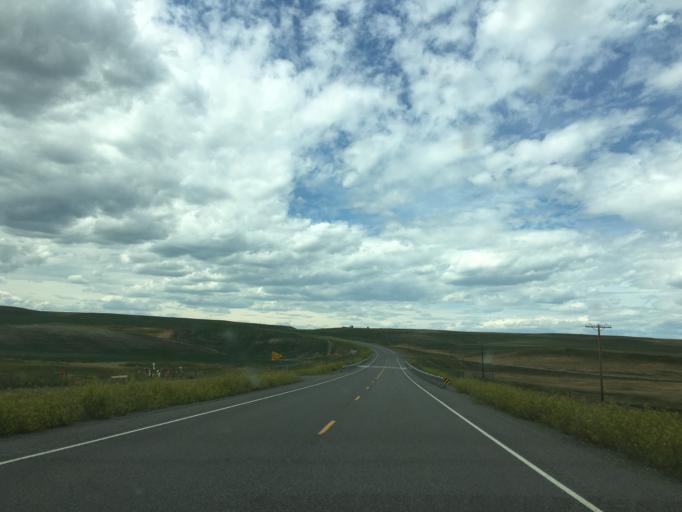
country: US
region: Montana
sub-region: Teton County
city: Choteau
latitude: 48.0849
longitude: -112.3380
